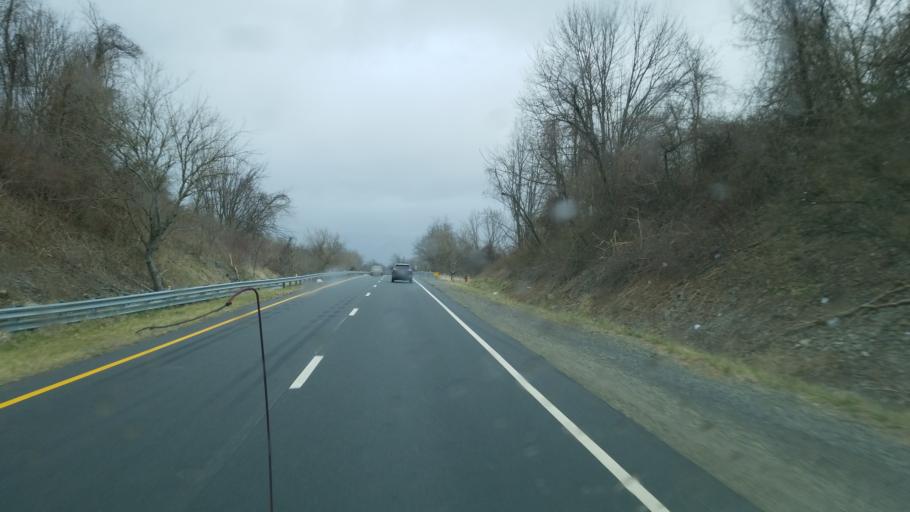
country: US
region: Virginia
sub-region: Giles County
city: Pearisburg
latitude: 37.2973
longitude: -80.7400
